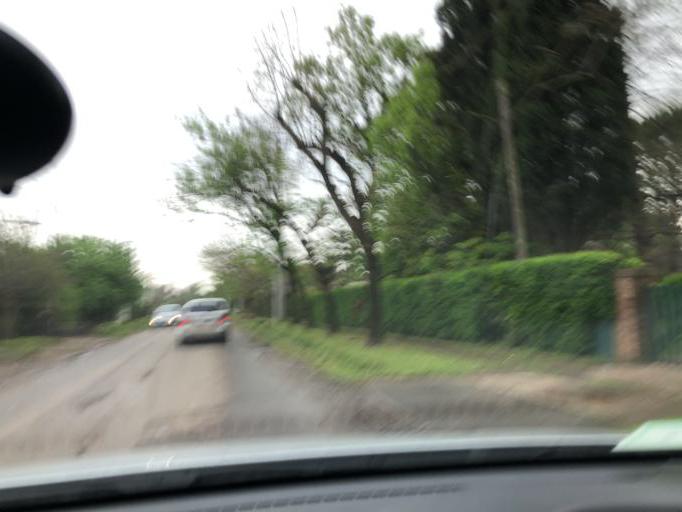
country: AR
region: Buenos Aires
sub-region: Partido de La Plata
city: La Plata
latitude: -34.8913
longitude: -58.0639
